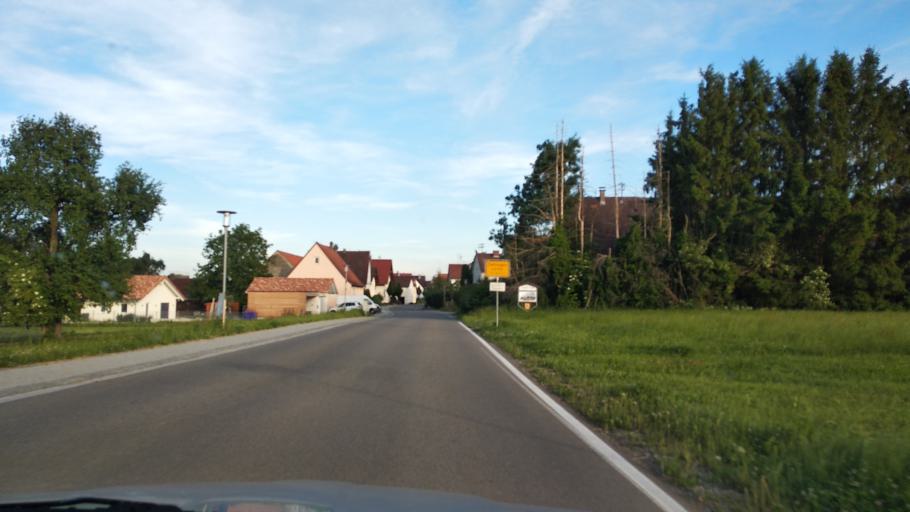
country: DE
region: Baden-Wuerttemberg
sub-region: Tuebingen Region
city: Dettingen an der Iller
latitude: 48.1116
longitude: 10.1067
